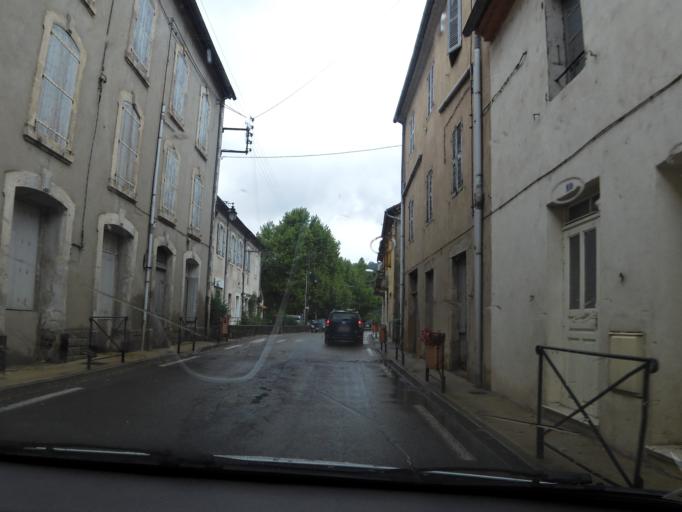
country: FR
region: Languedoc-Roussillon
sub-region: Departement du Gard
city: Branoux-les-Taillades
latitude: 44.2272
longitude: 4.0099
